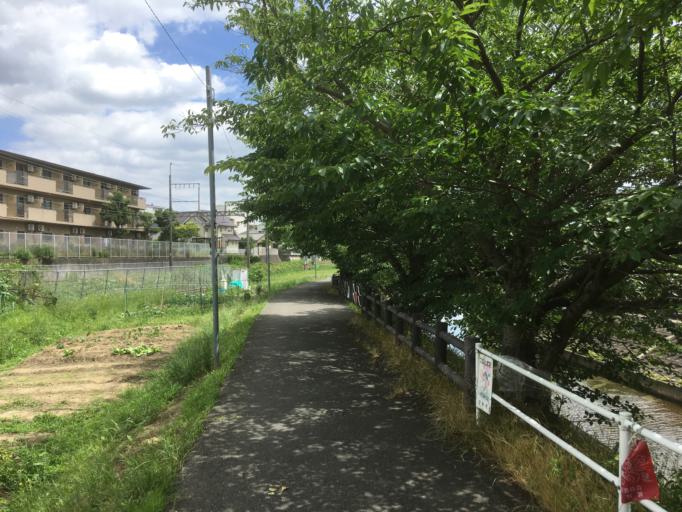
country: JP
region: Nara
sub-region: Ikoma-shi
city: Ikoma
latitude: 34.6825
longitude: 135.7070
